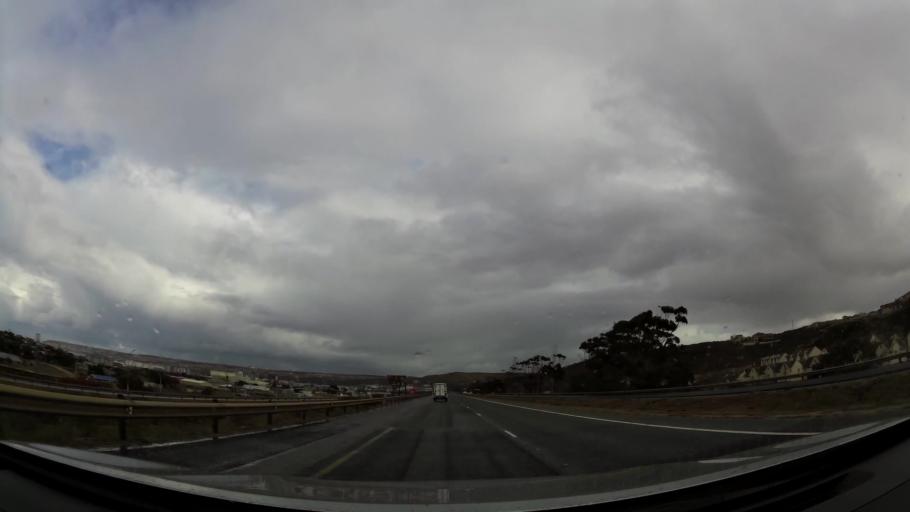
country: ZA
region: Western Cape
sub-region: Eden District Municipality
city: Mossel Bay
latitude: -34.1361
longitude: 22.1015
